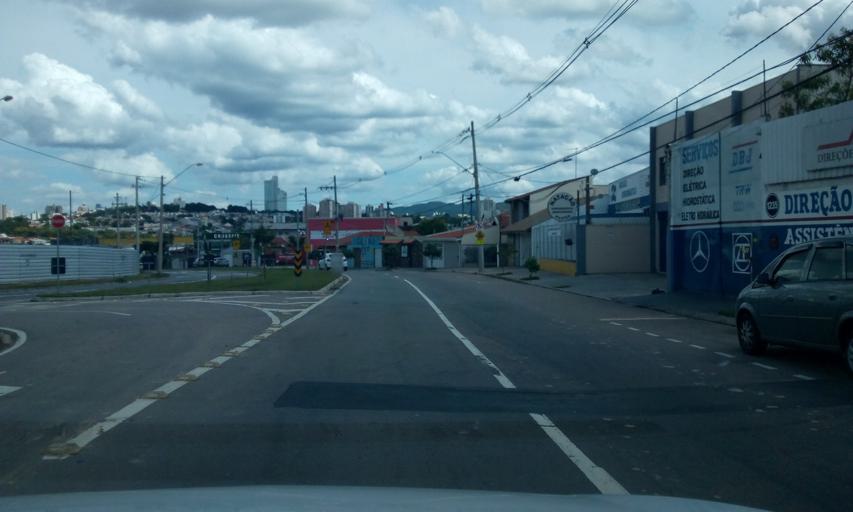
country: BR
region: Sao Paulo
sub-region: Jundiai
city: Jundiai
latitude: -23.1678
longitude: -46.8951
